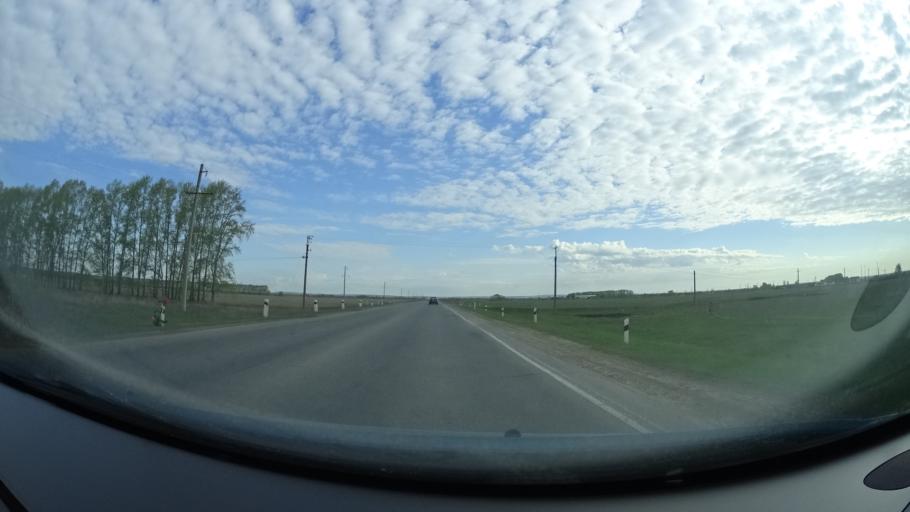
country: RU
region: Bashkortostan
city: Mikhaylovka
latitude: 54.9584
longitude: 55.7579
